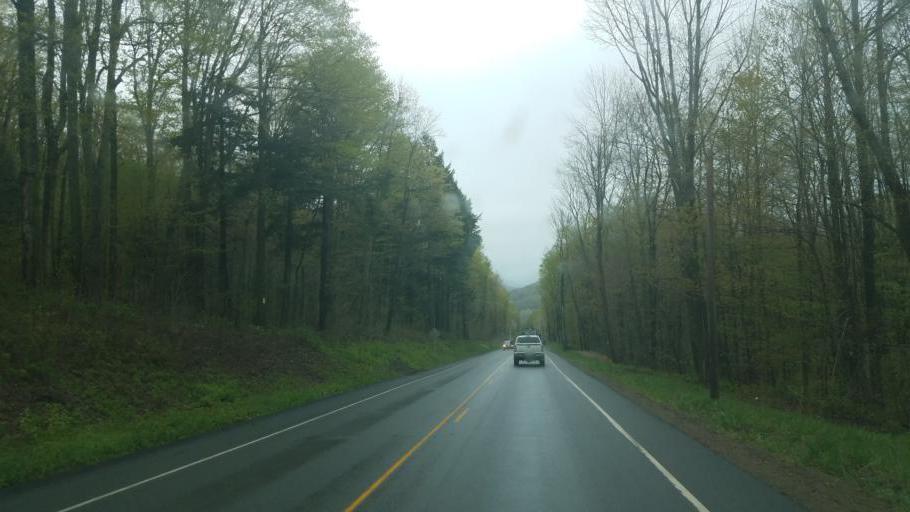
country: US
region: Pennsylvania
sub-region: McKean County
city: Smethport
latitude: 41.8230
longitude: -78.3881
